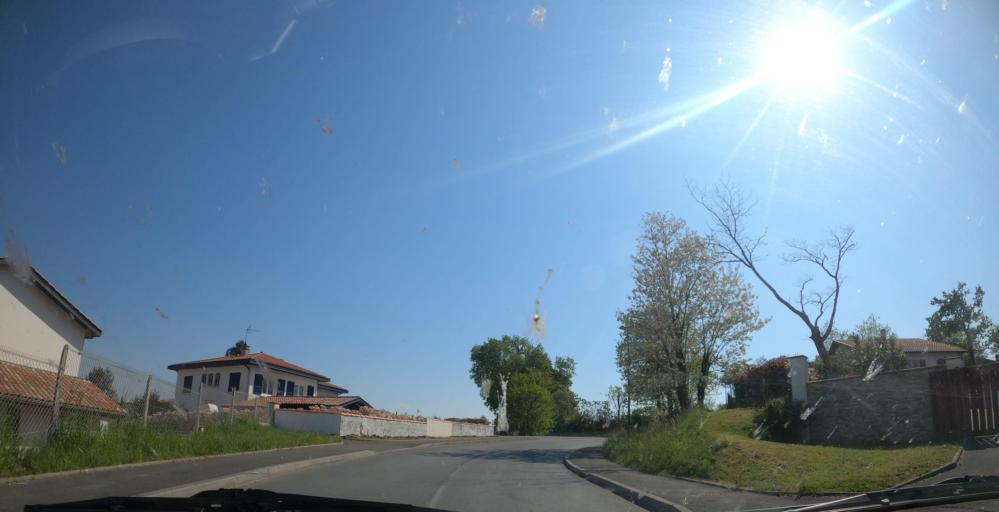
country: FR
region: Aquitaine
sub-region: Departement des Pyrenees-Atlantiques
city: Bassussarry
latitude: 43.4458
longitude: -1.5014
